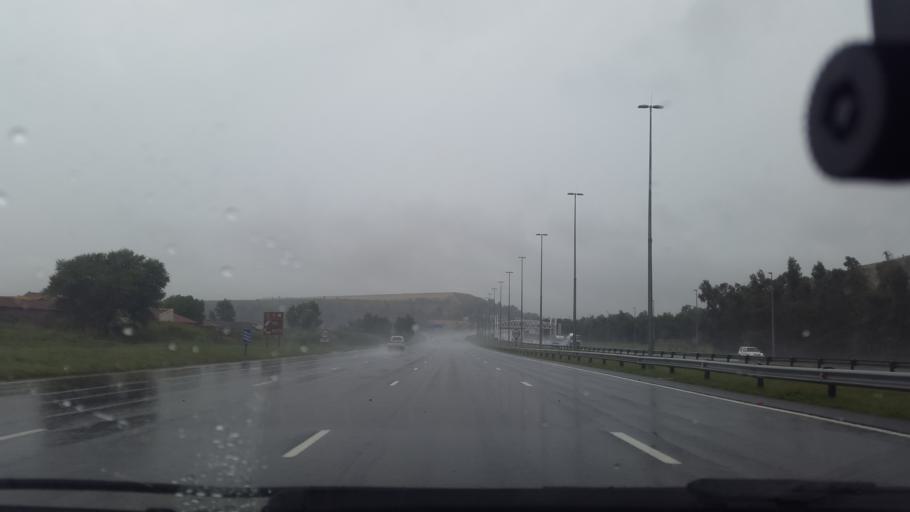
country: ZA
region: Gauteng
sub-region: City of Johannesburg Metropolitan Municipality
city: Johannesburg
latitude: -26.2417
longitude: 27.9620
